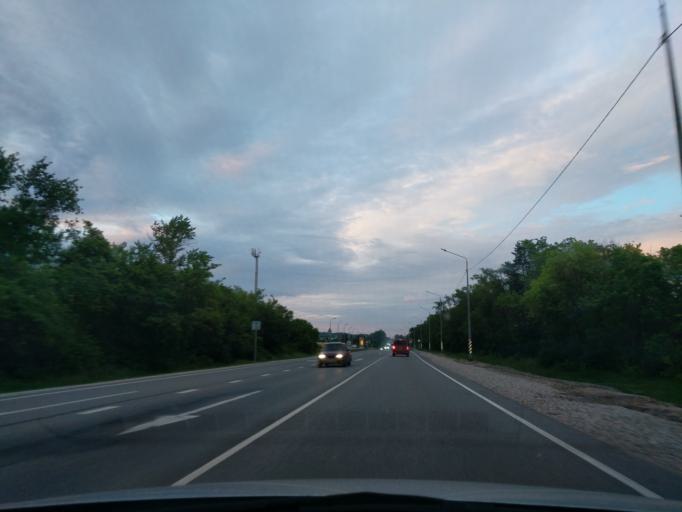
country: RU
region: Kaluga
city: Obninsk
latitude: 55.0680
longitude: 36.6045
